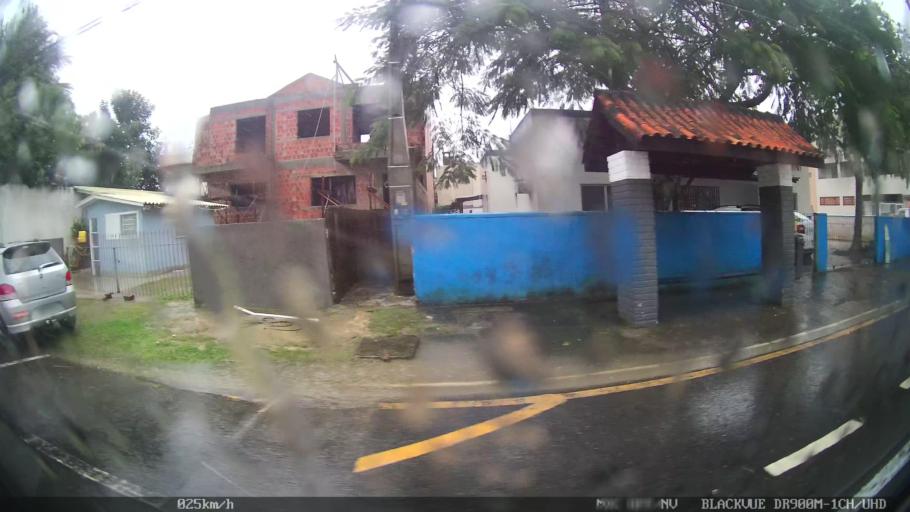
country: BR
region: Santa Catarina
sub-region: Balneario Camboriu
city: Balneario Camboriu
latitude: -27.0144
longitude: -48.6322
